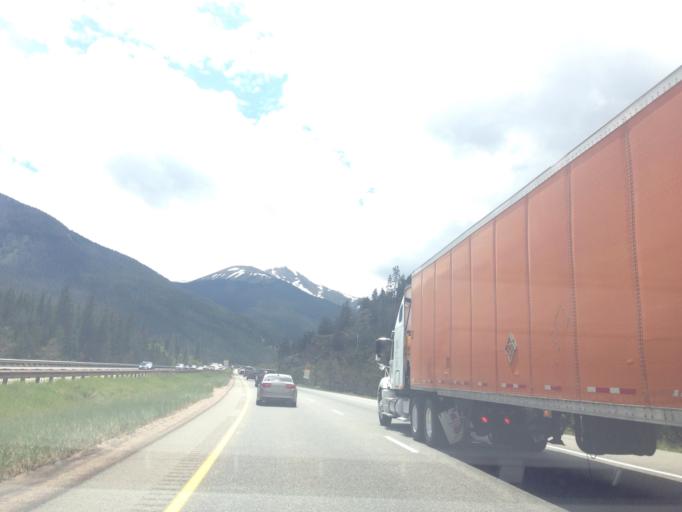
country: US
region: Colorado
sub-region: Clear Creek County
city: Georgetown
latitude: 39.6957
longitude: -105.7950
